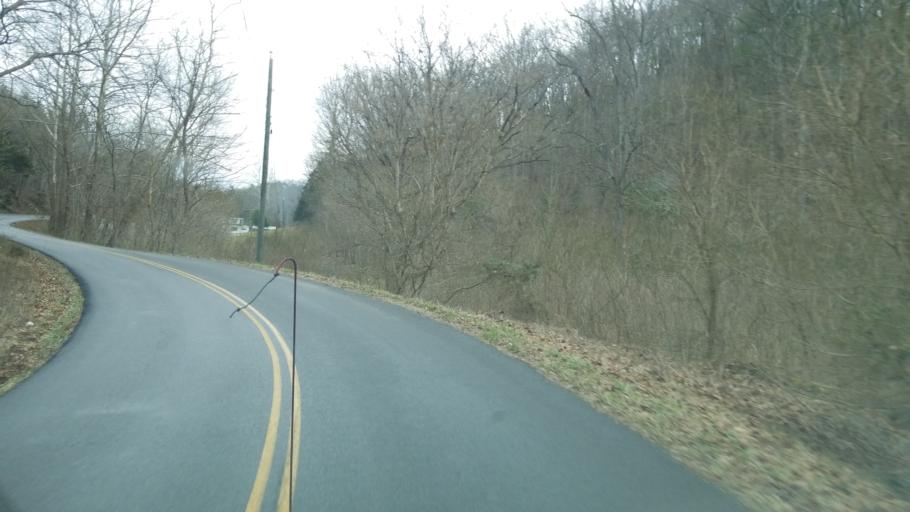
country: US
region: Virginia
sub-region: Giles County
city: Pearisburg
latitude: 37.2463
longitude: -80.6952
